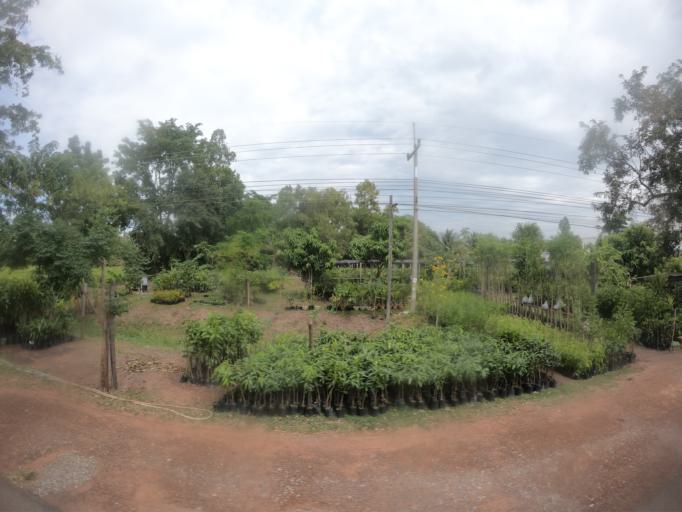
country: TH
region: Maha Sarakham
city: Chiang Yuen
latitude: 16.3375
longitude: 103.1666
